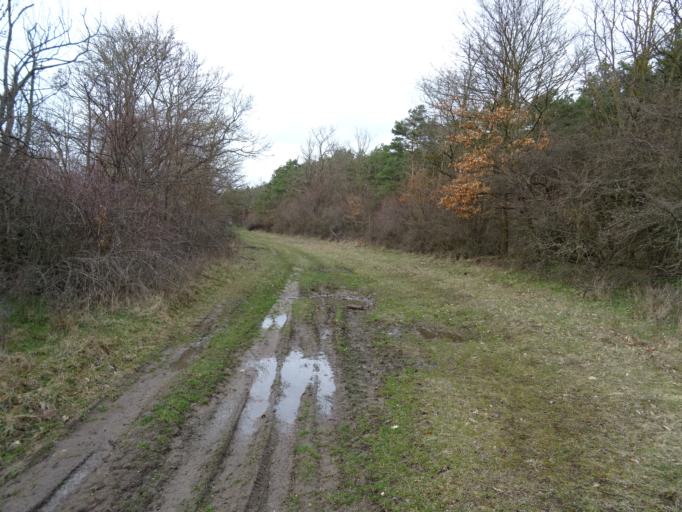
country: HU
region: Gyor-Moson-Sopron
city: Fertoszentmiklos
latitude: 47.4894
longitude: 16.9266
